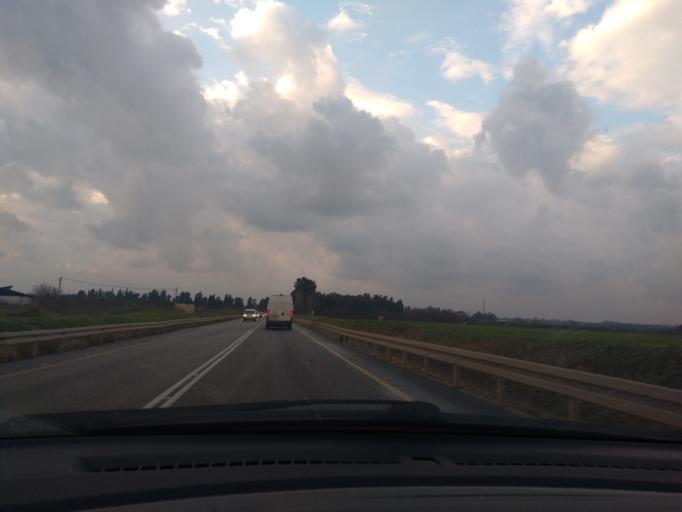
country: IL
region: Central District
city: Elyakhin
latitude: 32.3752
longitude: 34.9015
